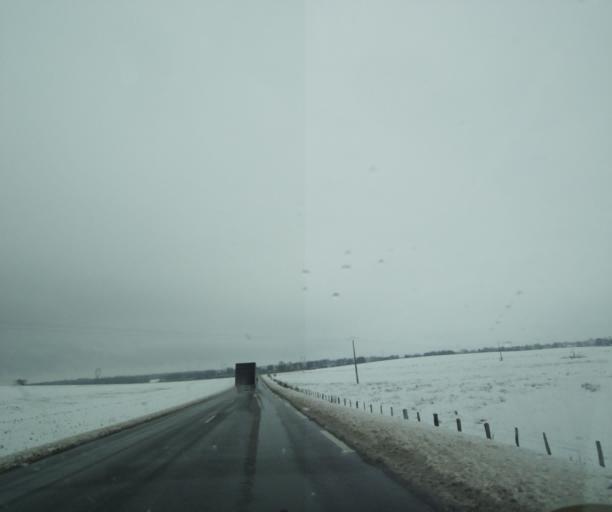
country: FR
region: Champagne-Ardenne
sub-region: Departement de la Haute-Marne
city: Montier-en-Der
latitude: 48.5137
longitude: 4.8052
